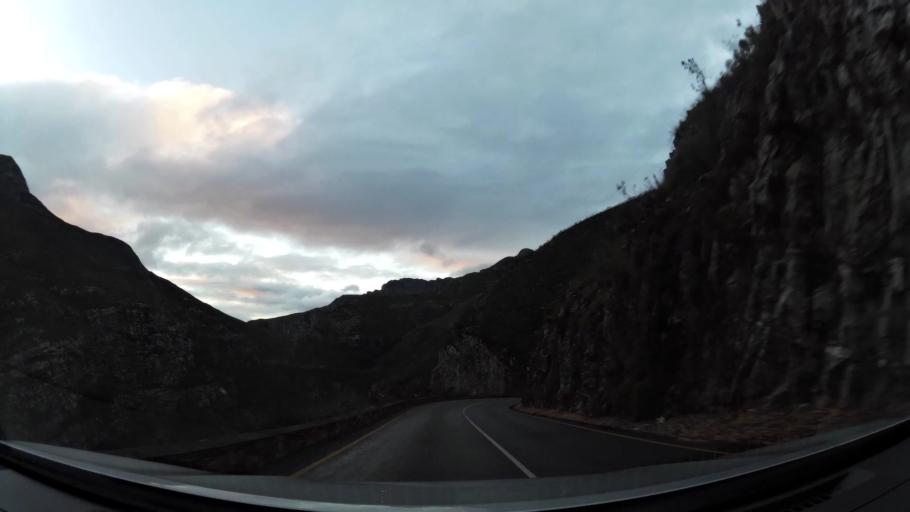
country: ZA
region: Western Cape
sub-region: Overberg District Municipality
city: Swellendam
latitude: -33.9725
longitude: 20.7005
